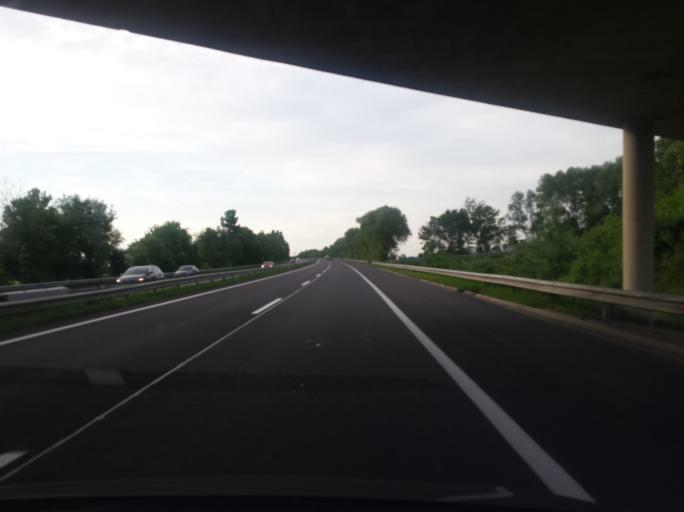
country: AT
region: Burgenland
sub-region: Eisenstadt-Umgebung
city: Wimpassing an der Leitha
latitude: 47.9072
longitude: 16.4115
